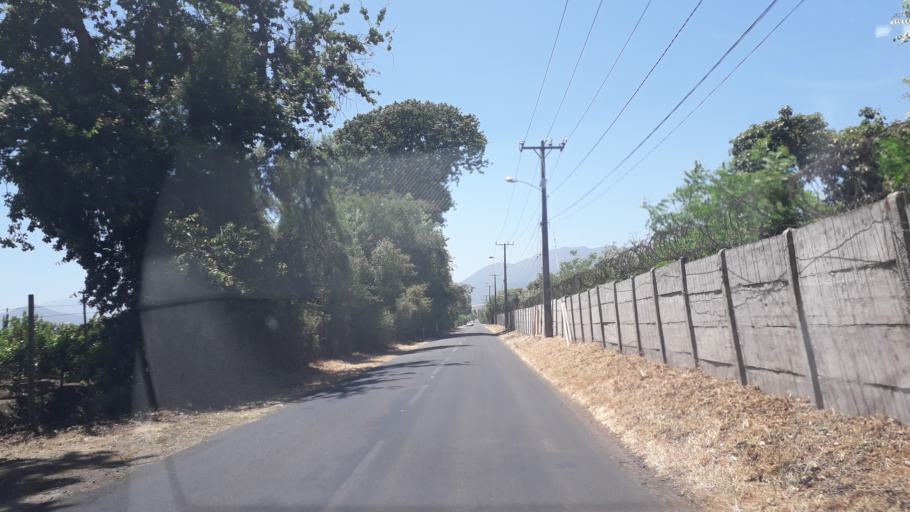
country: CL
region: Valparaiso
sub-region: Provincia de Quillota
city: Quillota
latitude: -32.9264
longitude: -71.2500
